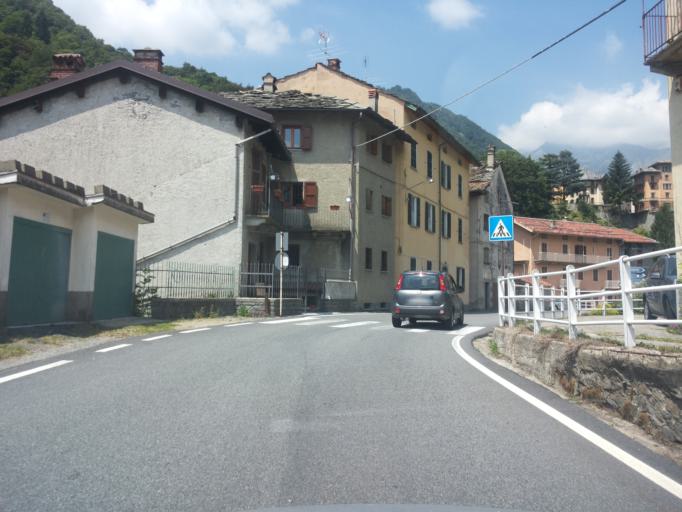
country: IT
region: Piedmont
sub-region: Provincia di Biella
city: Rosazza
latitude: 45.6731
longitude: 7.9835
